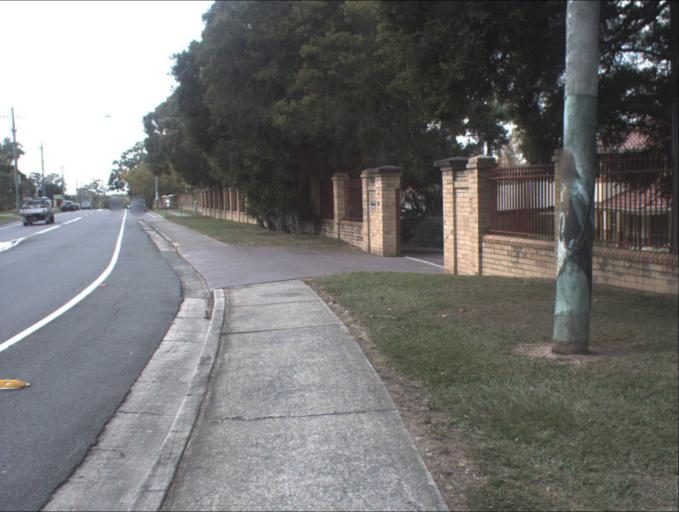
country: AU
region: Queensland
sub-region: Logan
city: Park Ridge South
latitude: -27.6875
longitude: 153.0291
